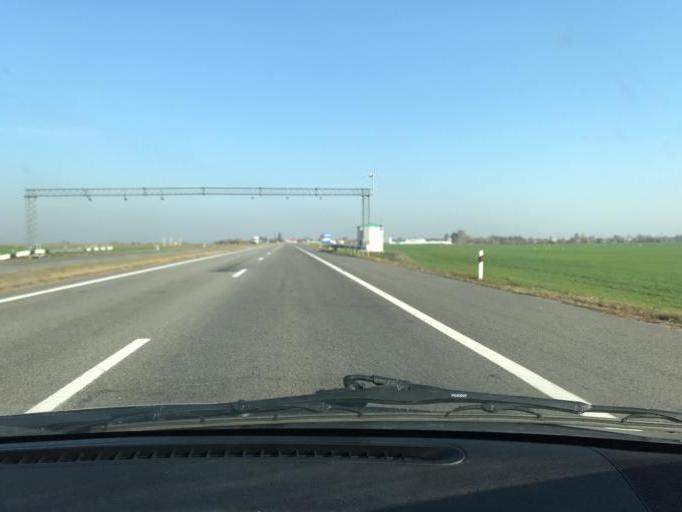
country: BY
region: Vitebsk
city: Horad Orsha
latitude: 54.5969
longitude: 30.3512
